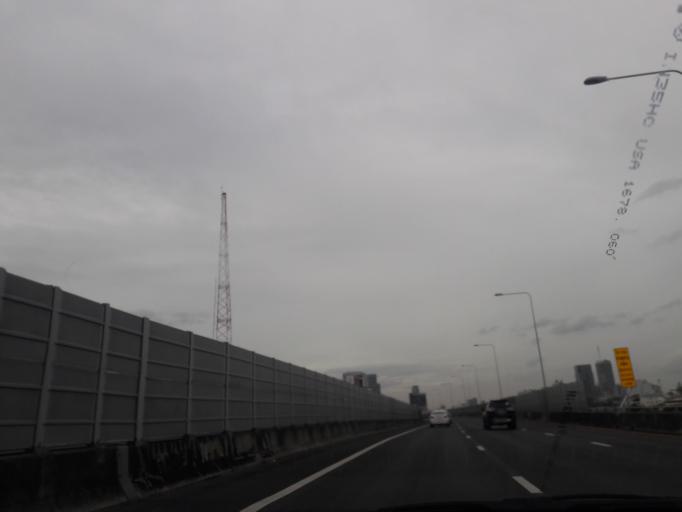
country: TH
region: Bangkok
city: Dusit
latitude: 13.7725
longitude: 100.5291
